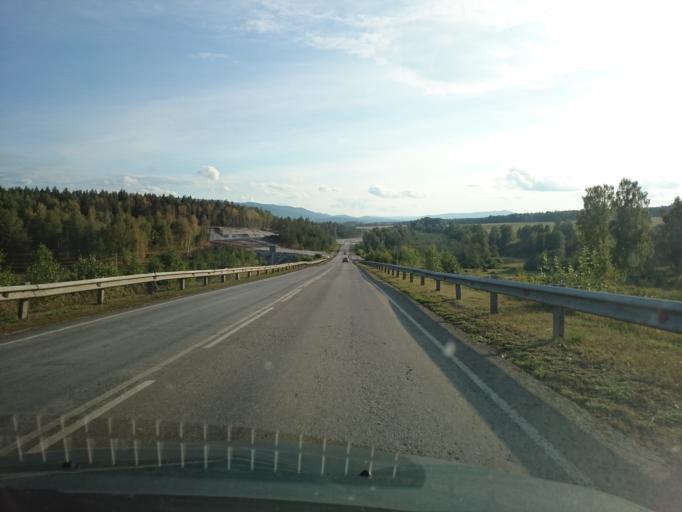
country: RU
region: Bashkortostan
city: Lomovka
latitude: 53.9141
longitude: 58.1835
